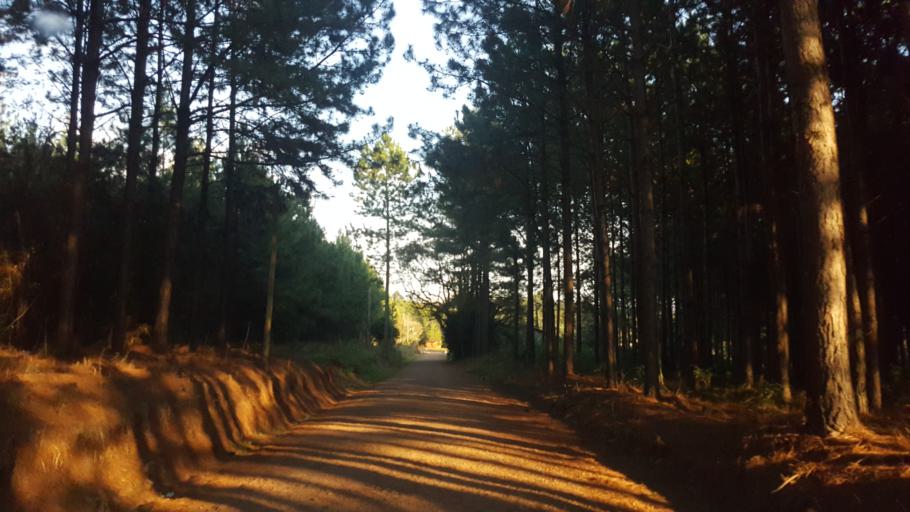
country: AR
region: Misiones
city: Capiovi
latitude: -26.8990
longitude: -55.0568
